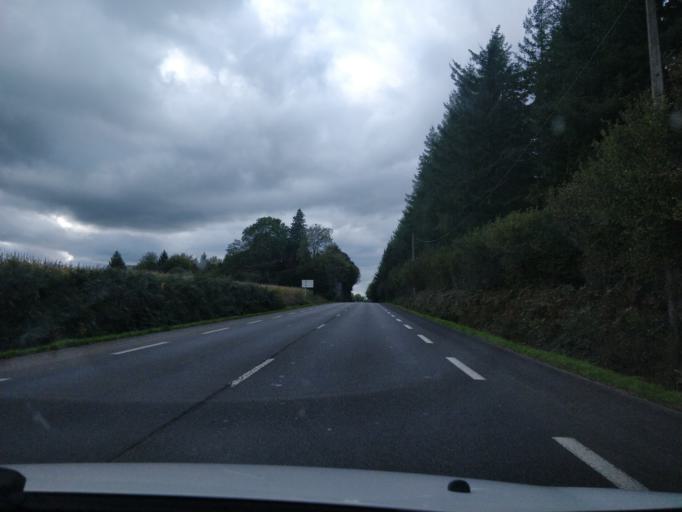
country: FR
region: Lower Normandy
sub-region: Departement du Calvados
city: Saint-Sever-Calvados
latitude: 48.8254
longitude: -1.0981
